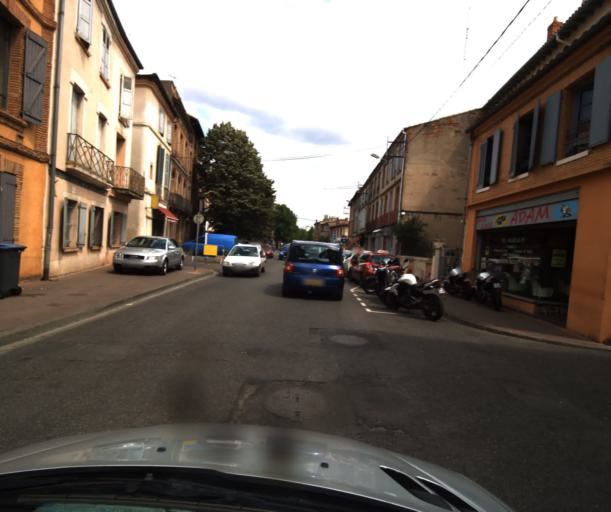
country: FR
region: Midi-Pyrenees
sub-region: Departement du Tarn-et-Garonne
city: Montauban
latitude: 44.0216
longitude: 1.3555
